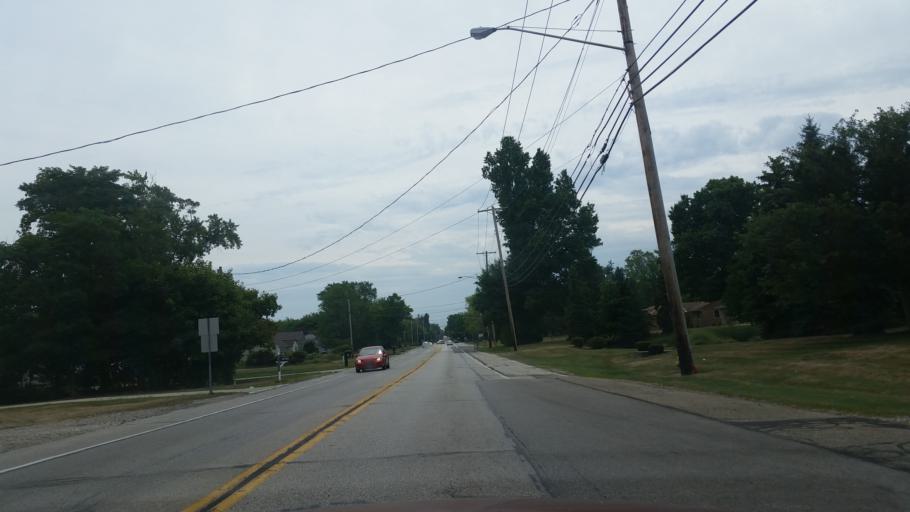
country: US
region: Ohio
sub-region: Cuyahoga County
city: Solon
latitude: 41.3780
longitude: -81.4248
